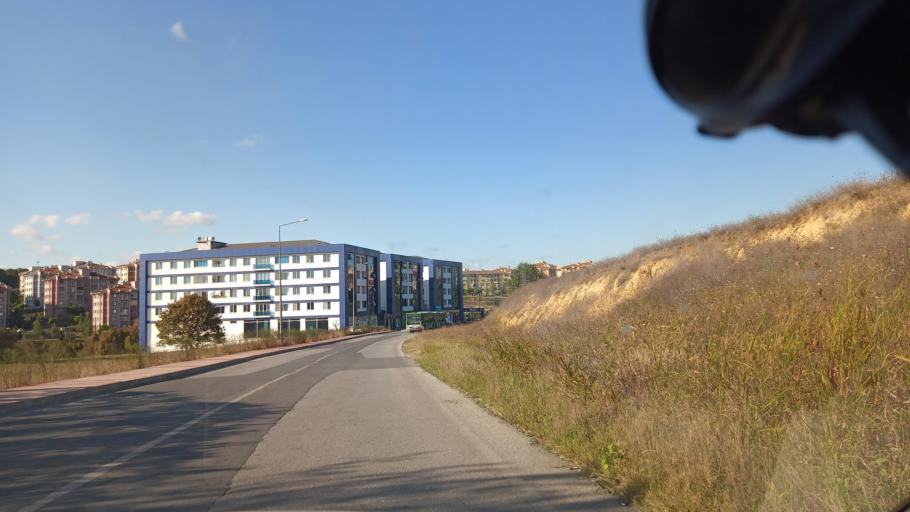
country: TR
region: Kocaeli
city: Kaymaz
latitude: 40.8571
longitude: 30.2771
